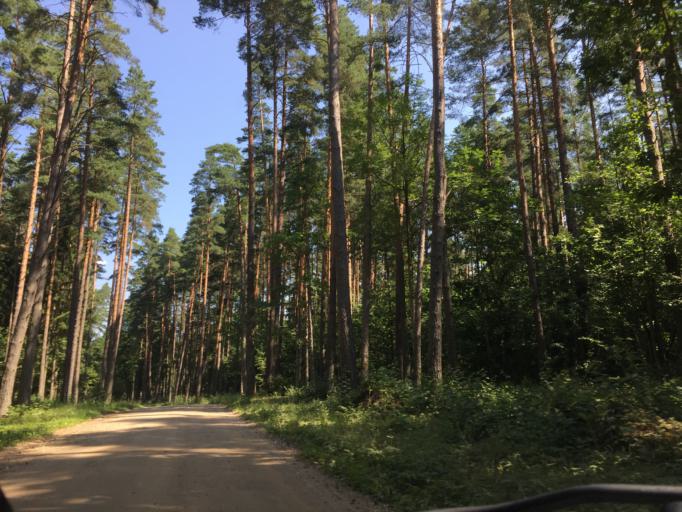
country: LV
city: Tervete
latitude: 56.4913
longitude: 23.4040
